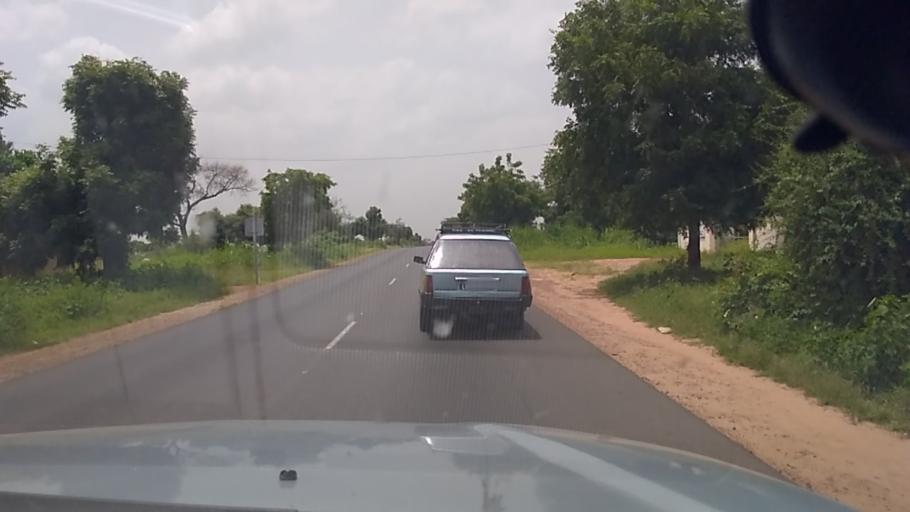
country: SN
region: Thies
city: Mekhe
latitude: 14.9862
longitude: -16.7601
